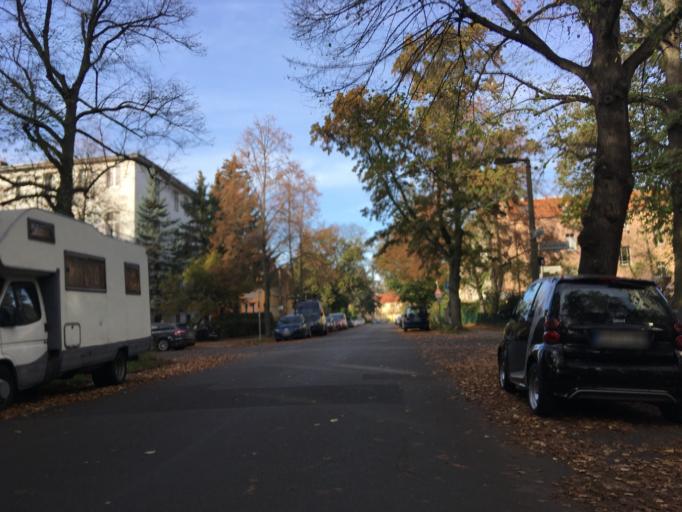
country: DE
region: Berlin
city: Niederschonhausen
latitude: 52.5866
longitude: 13.3973
